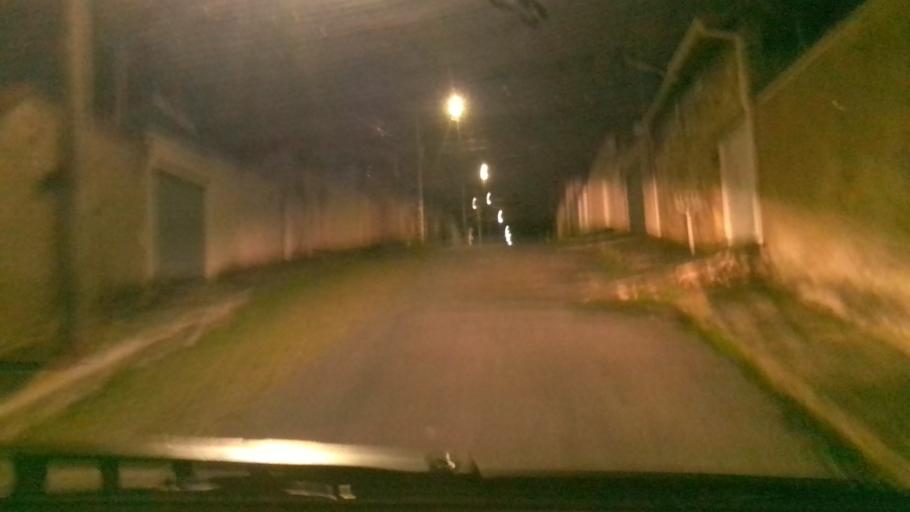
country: BR
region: Minas Gerais
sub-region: Belo Horizonte
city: Belo Horizonte
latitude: -19.9095
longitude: -43.9002
